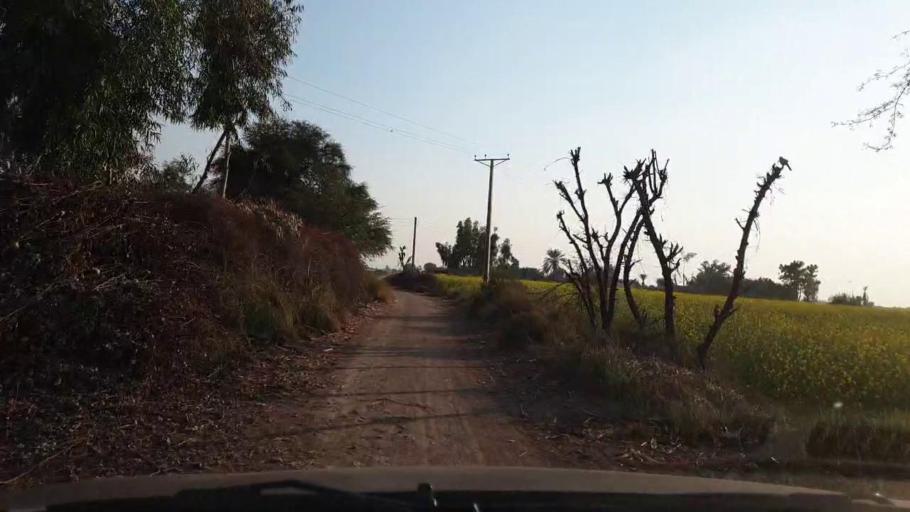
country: PK
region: Sindh
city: Jhol
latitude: 25.9279
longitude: 68.9176
